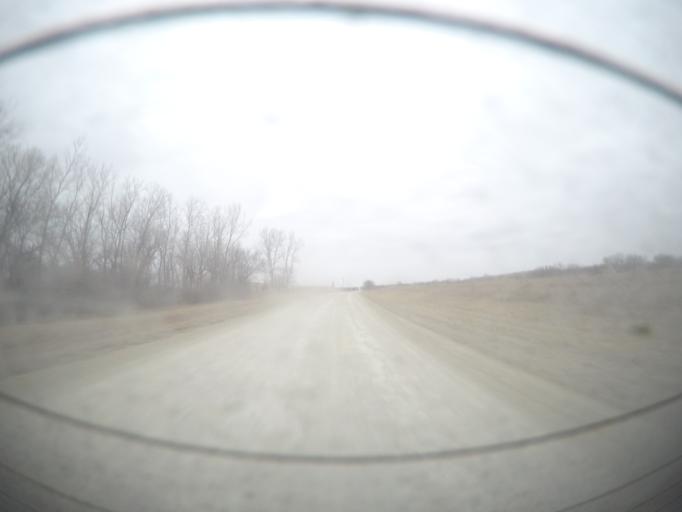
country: US
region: Kansas
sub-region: Wabaunsee County
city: Alma
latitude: 39.0683
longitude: -96.2424
